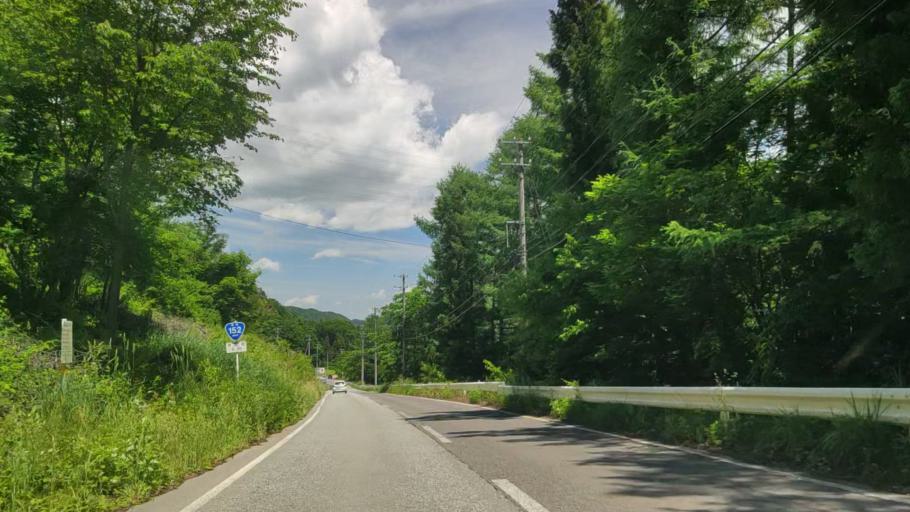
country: JP
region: Nagano
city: Kamimaruko
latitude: 36.1881
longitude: 138.2443
